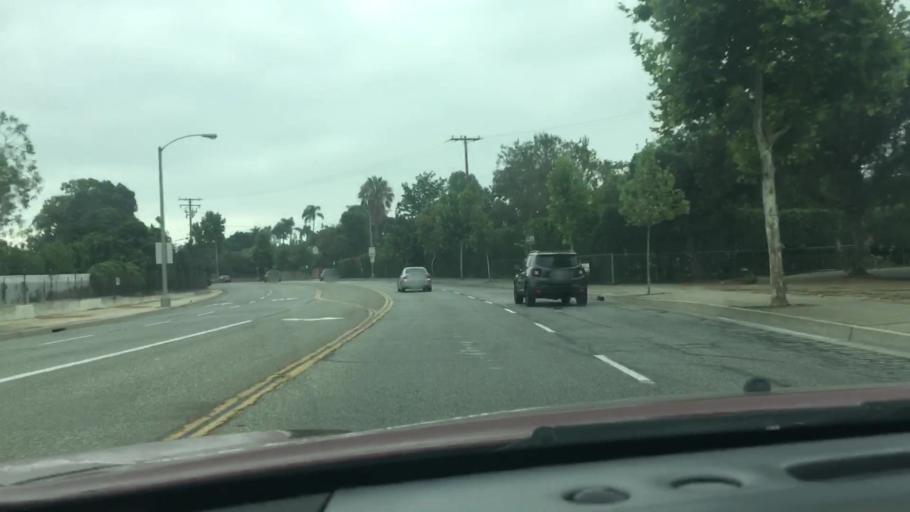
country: US
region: California
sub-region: Orange County
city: Fullerton
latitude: 33.8742
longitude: -117.9373
